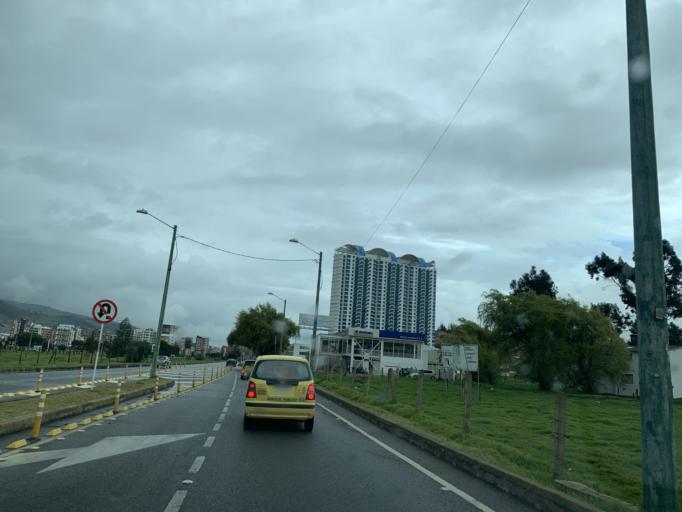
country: CO
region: Boyaca
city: Tunja
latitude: 5.5366
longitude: -73.3527
